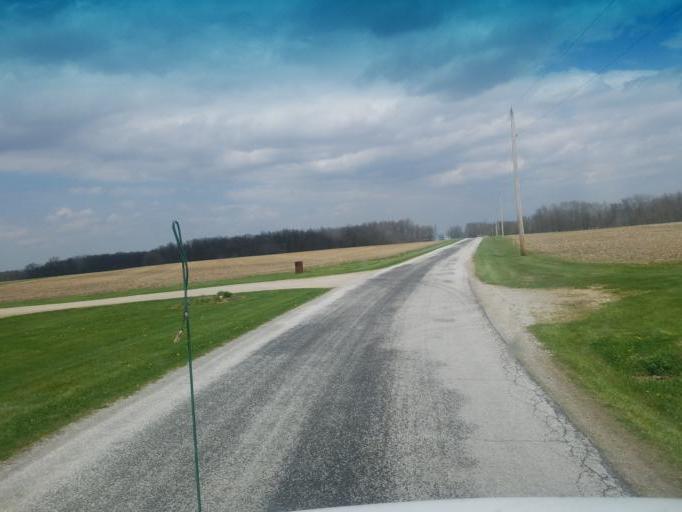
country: US
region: Ohio
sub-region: Wyandot County
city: Upper Sandusky
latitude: 40.9140
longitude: -83.2588
